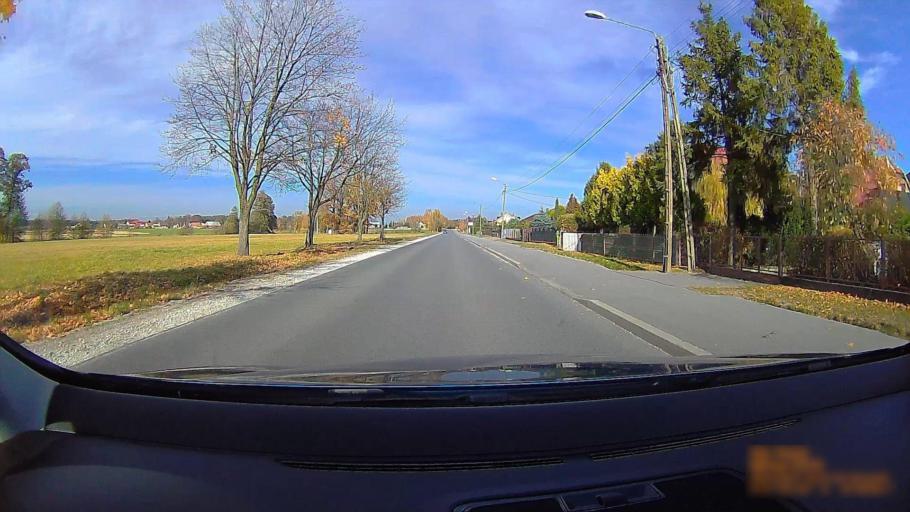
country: PL
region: Greater Poland Voivodeship
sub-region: Powiat kepinski
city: Kepno
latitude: 51.3176
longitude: 18.0139
